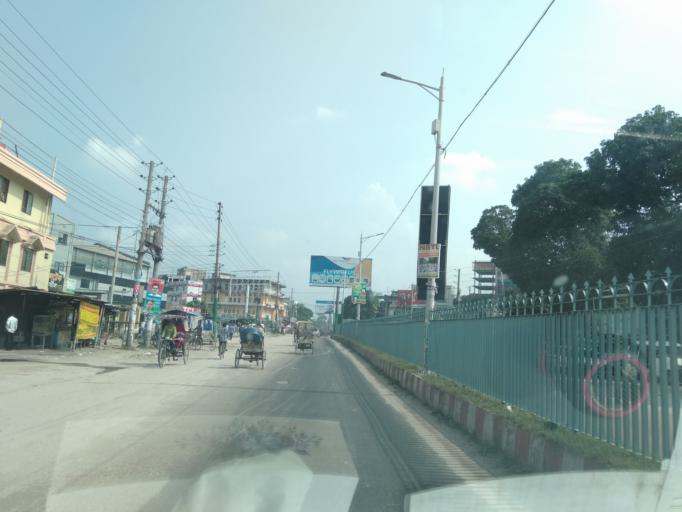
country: BD
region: Rangpur Division
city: Rangpur
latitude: 25.7617
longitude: 89.2315
